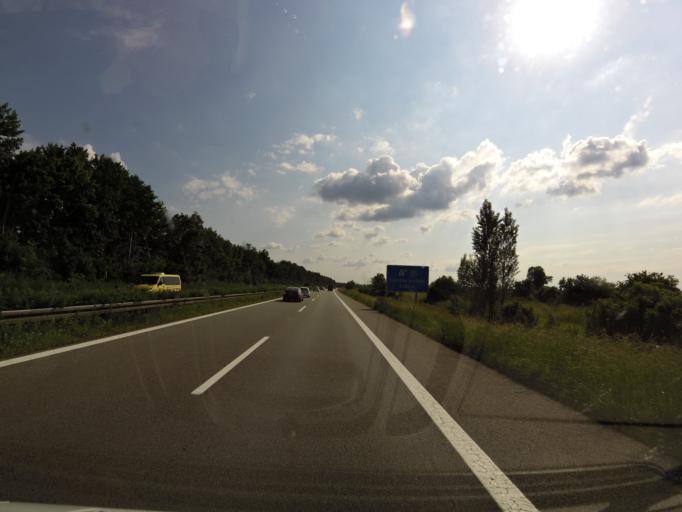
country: DE
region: Bavaria
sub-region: Lower Bavaria
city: Landau an der Isar
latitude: 48.7032
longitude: 12.6873
